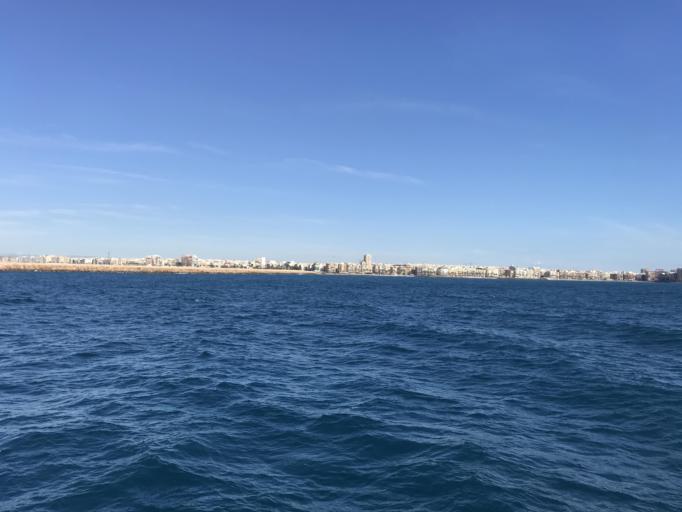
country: ES
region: Valencia
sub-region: Provincia de Alicante
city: Torrevieja
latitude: 37.9630
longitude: -0.6778
